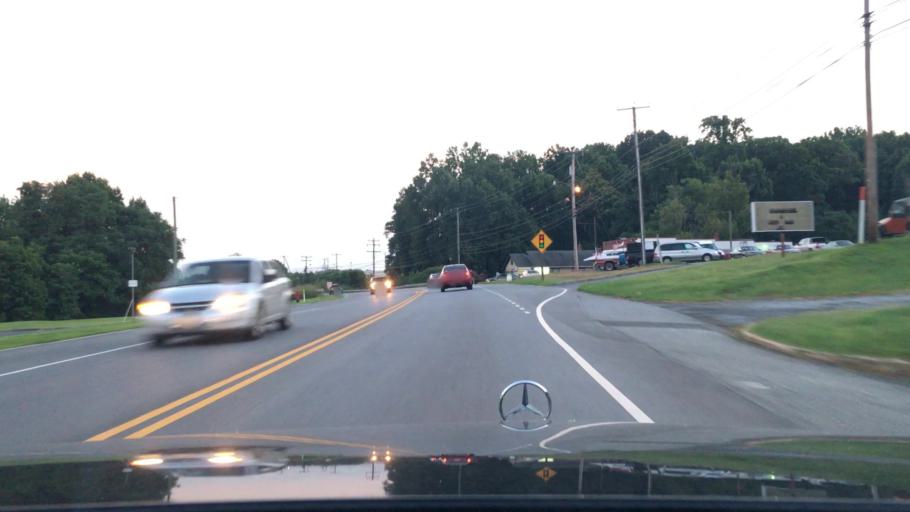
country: US
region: Virginia
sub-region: Campbell County
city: Altavista
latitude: 37.1241
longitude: -79.2729
